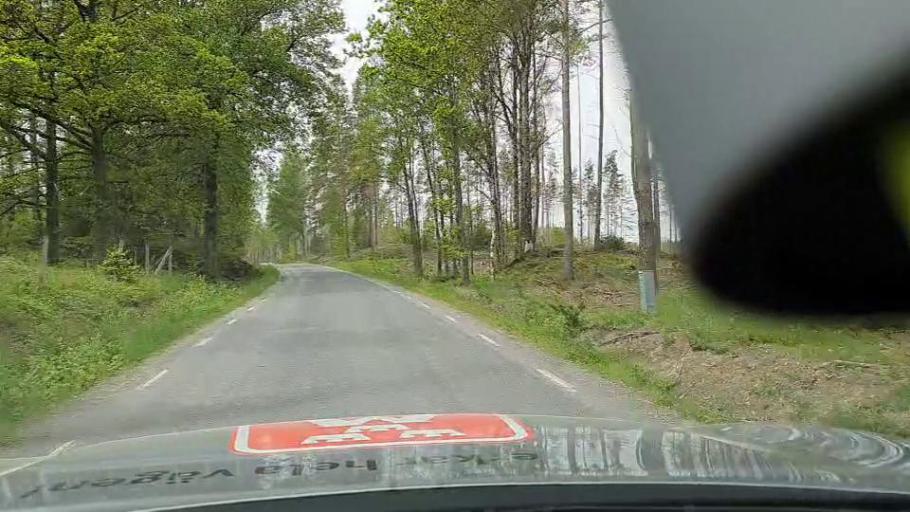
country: SE
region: Soedermanland
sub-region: Flens Kommun
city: Halleforsnas
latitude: 59.1022
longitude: 16.5154
